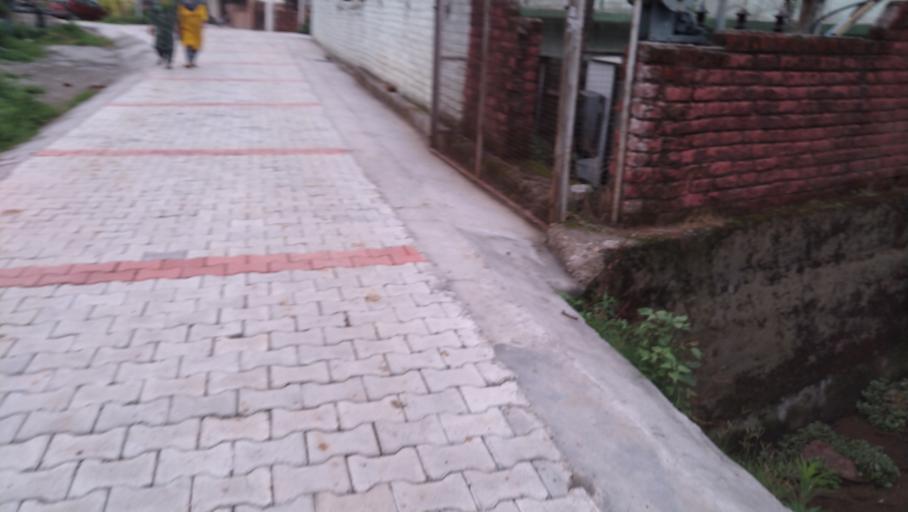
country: IN
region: Himachal Pradesh
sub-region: Kangra
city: Dharmsala
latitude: 32.1992
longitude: 76.3356
